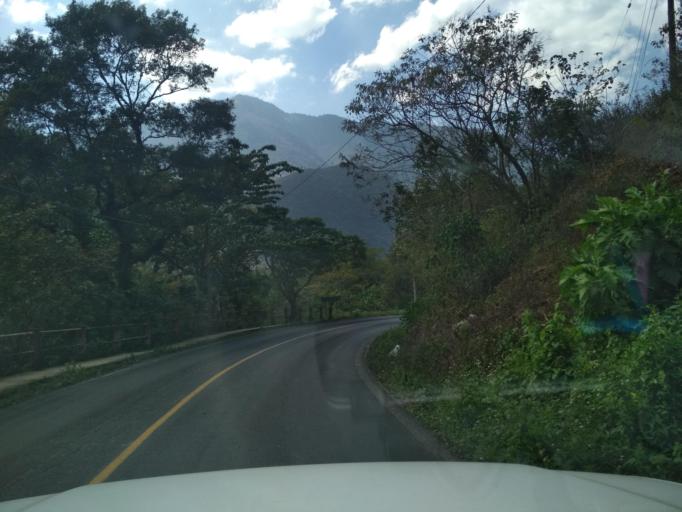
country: MX
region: Veracruz
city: Jalapilla
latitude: 18.7908
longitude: -97.0958
